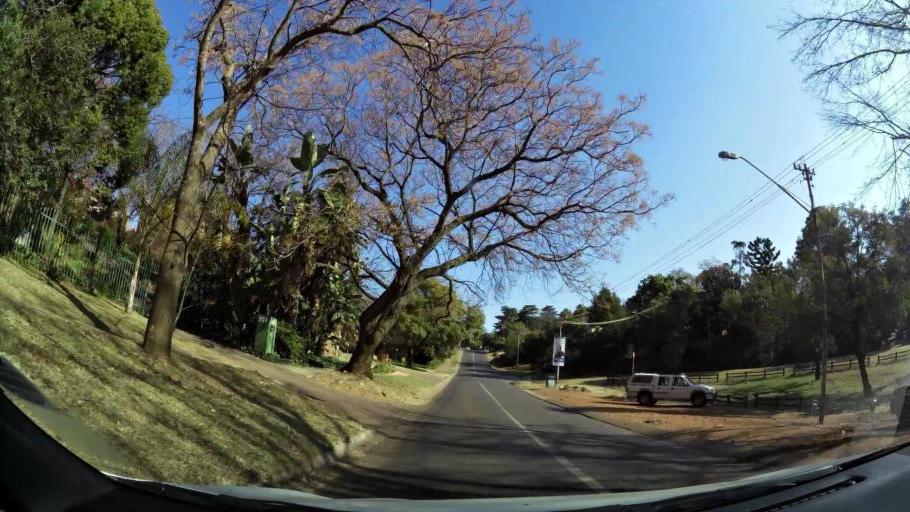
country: ZA
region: Gauteng
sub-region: City of Tshwane Metropolitan Municipality
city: Pretoria
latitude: -25.7935
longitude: 28.2431
